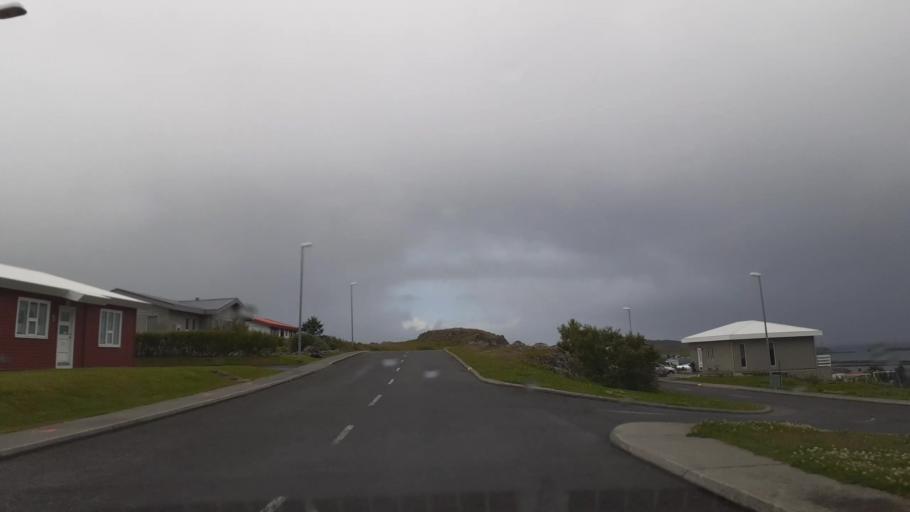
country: IS
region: East
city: Egilsstadir
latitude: 65.7533
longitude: -14.8333
